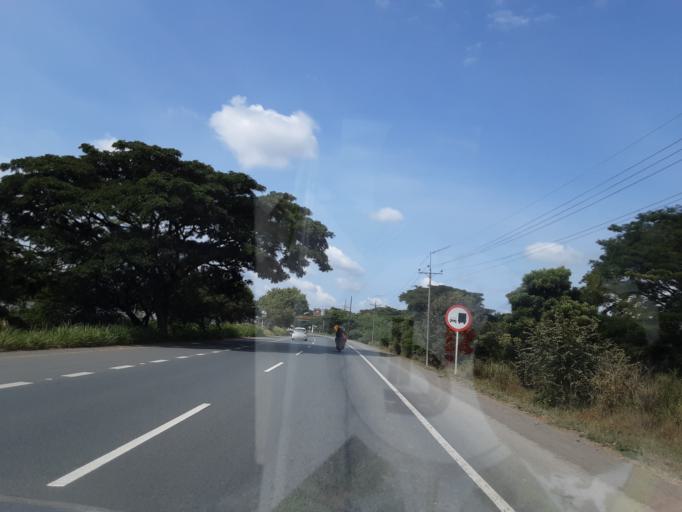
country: CO
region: Valle del Cauca
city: Guacari
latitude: 3.7703
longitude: -76.3270
